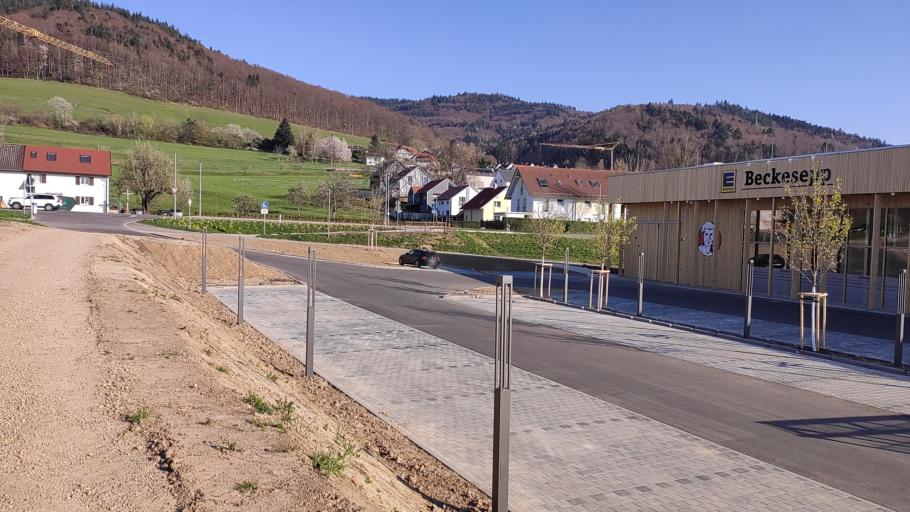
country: DE
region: Baden-Wuerttemberg
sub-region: Freiburg Region
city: Solden
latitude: 47.9357
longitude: 7.8116
